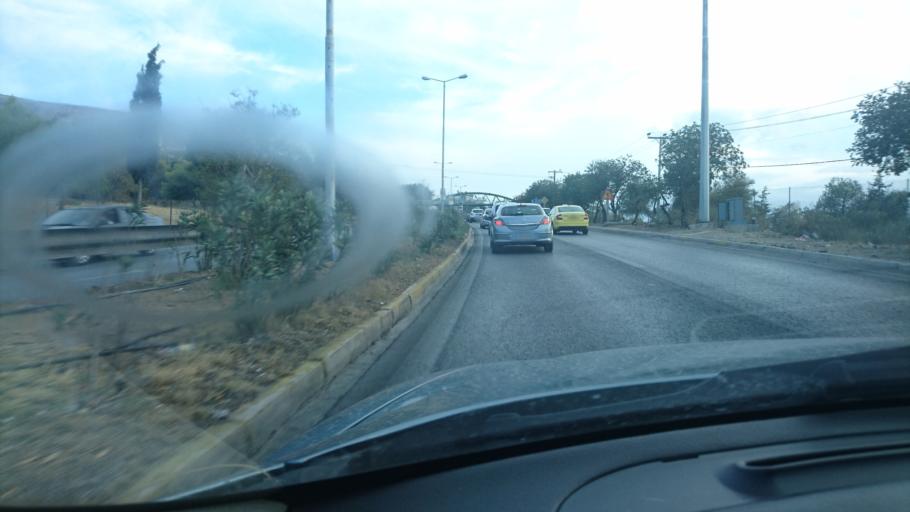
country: GR
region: Attica
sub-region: Nomarchia Athinas
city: Kaisariani
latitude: 37.9510
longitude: 23.7681
